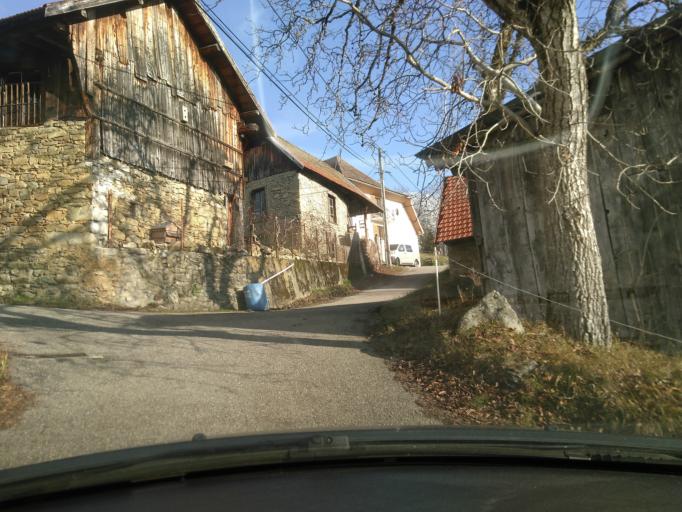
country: FR
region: Rhone-Alpes
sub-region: Departement de l'Isere
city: Froges
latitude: 45.2353
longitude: 5.9348
